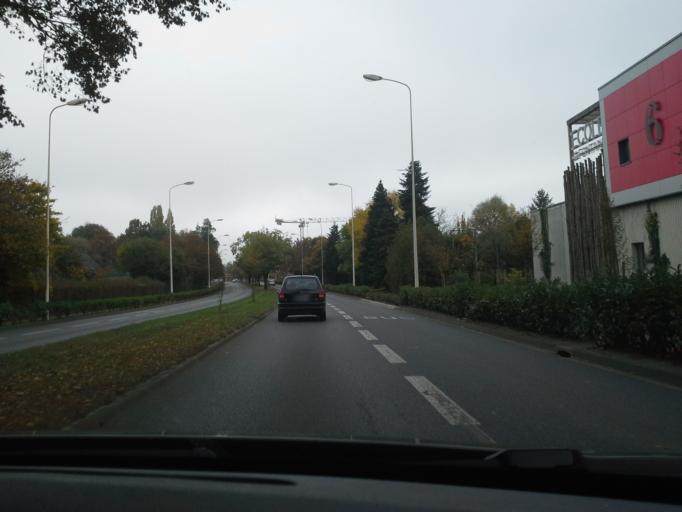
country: FR
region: Centre
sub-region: Departement d'Indre-et-Loire
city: Tours
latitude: 47.4166
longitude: 0.7037
